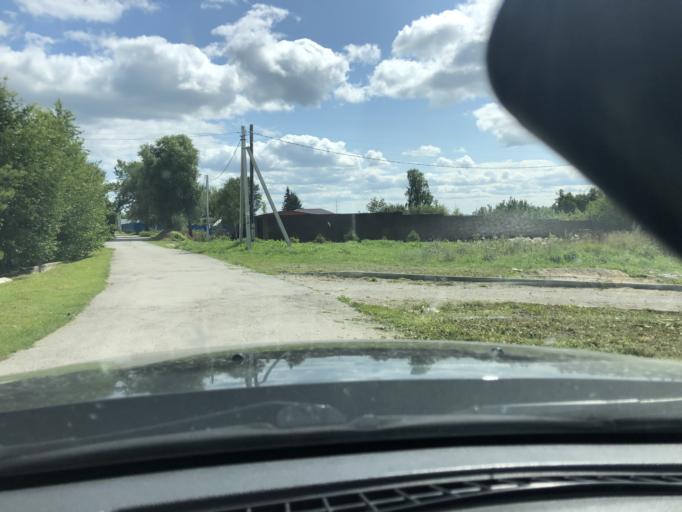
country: RU
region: Tula
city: Revyakino
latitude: 54.3490
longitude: 37.6157
